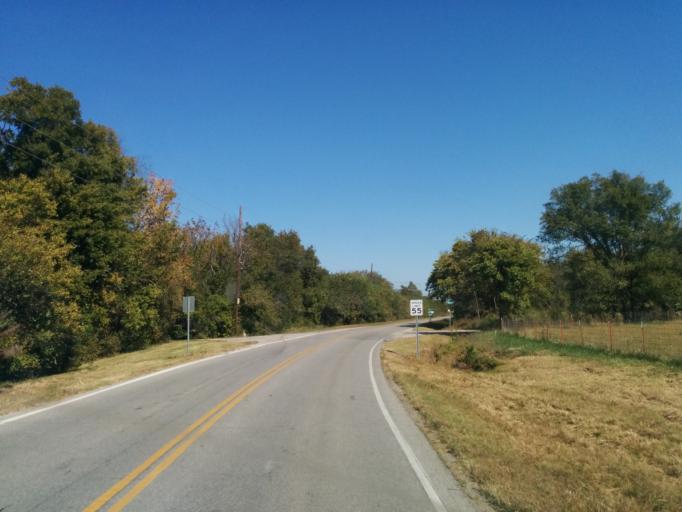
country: US
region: Oklahoma
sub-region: Creek County
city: Mounds
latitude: 35.8565
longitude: -96.0689
